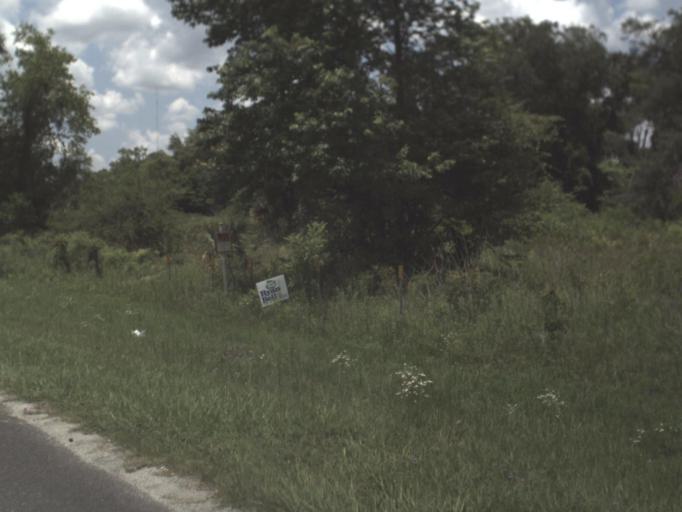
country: US
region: Florida
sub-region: Levy County
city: Manatee Road
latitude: 29.5913
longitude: -82.9256
